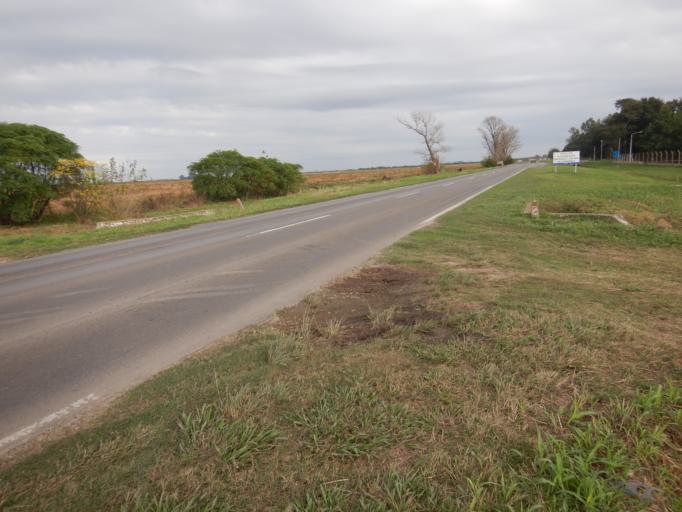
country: AR
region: Santa Fe
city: Roldan
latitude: -32.8923
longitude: -60.9821
